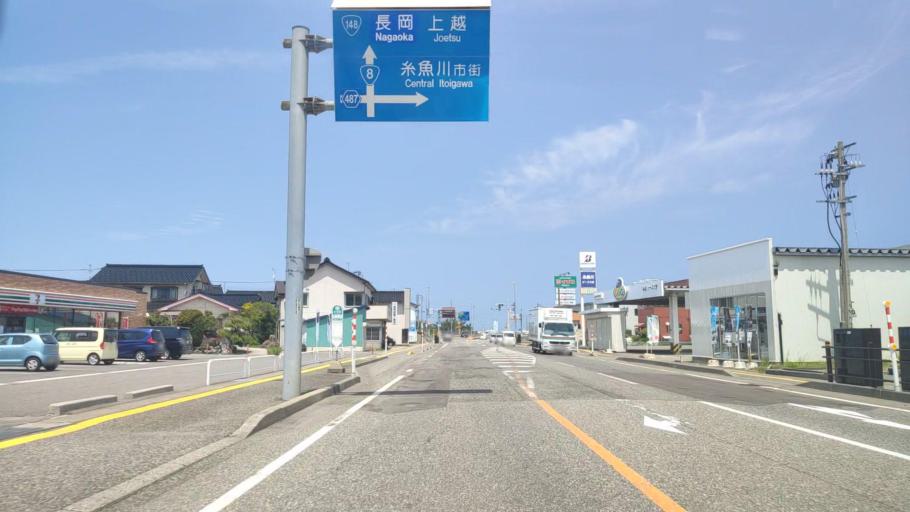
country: JP
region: Niigata
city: Itoigawa
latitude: 37.0410
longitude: 137.8466
